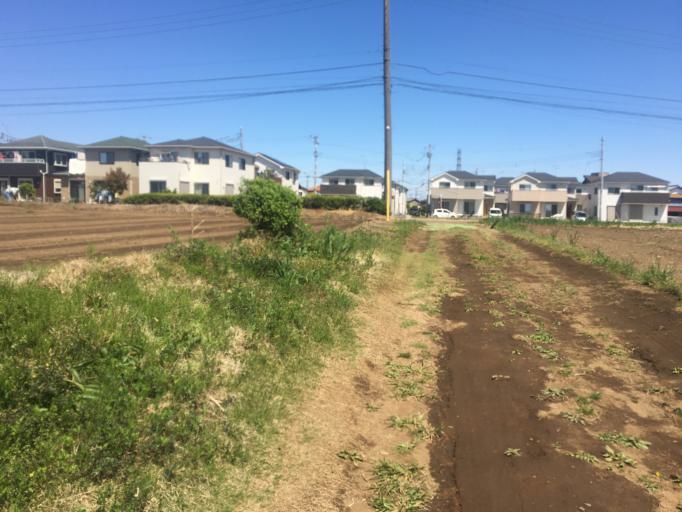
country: JP
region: Saitama
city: Shiki
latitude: 35.8384
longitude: 139.5630
